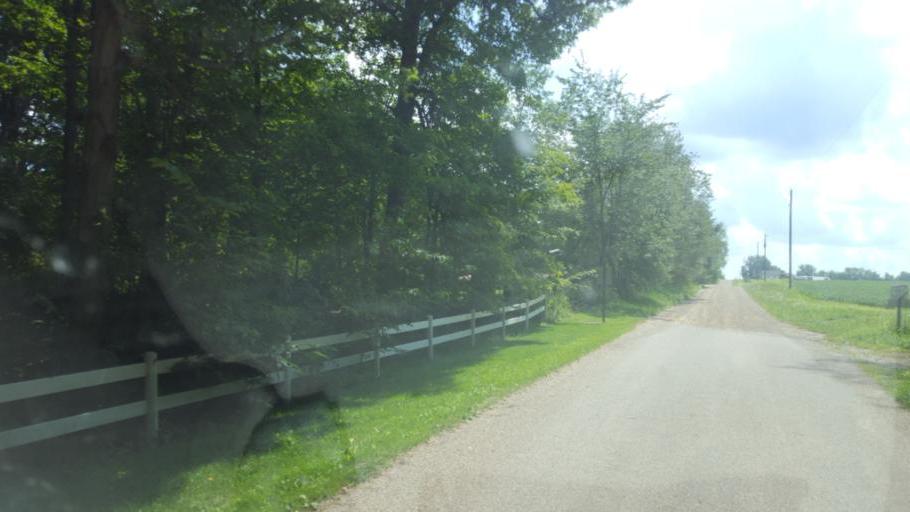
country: US
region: Ohio
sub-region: Knox County
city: Fredericktown
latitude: 40.4156
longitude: -82.5829
